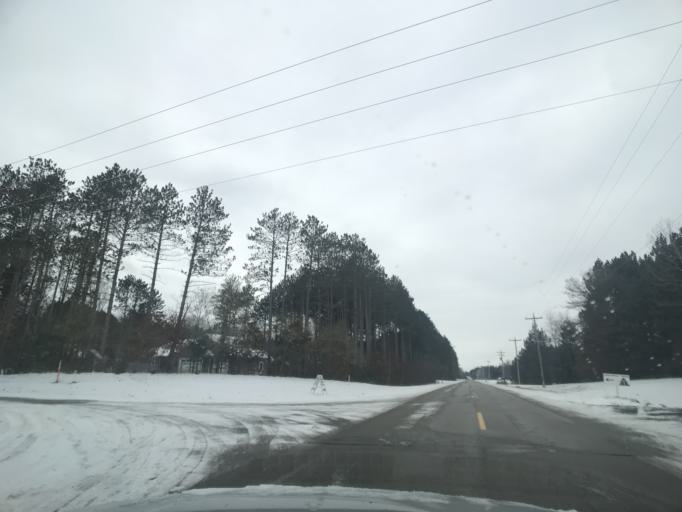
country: US
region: Wisconsin
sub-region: Brown County
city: Suamico
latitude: 44.7064
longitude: -88.1011
